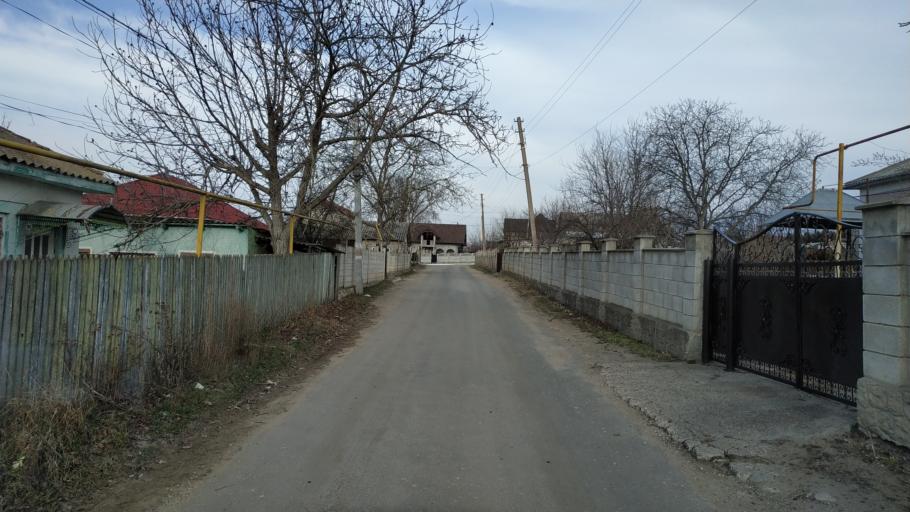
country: MD
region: Chisinau
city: Vatra
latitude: 46.9857
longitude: 28.6702
